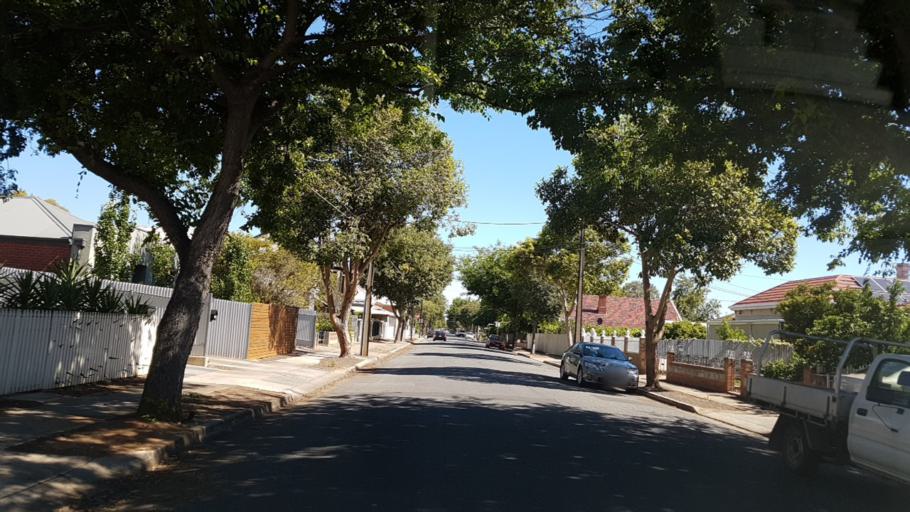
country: AU
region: South Australia
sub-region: City of West Torrens
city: Thebarton
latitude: -34.9174
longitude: 138.5608
